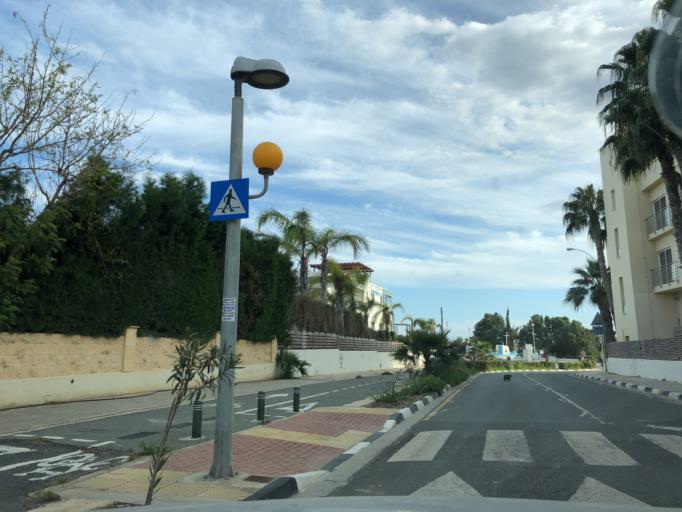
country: CY
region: Larnaka
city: Perivolia
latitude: 34.8182
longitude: 33.6019
